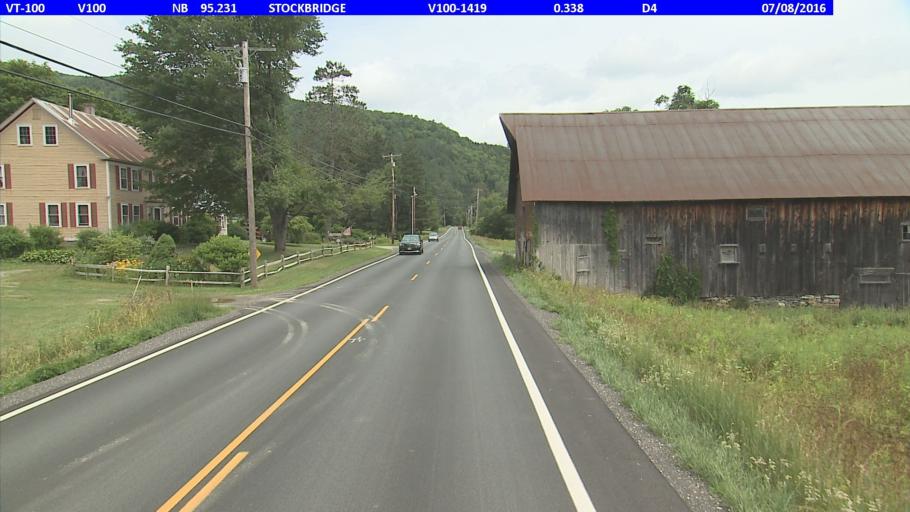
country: US
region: Vermont
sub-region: Orange County
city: Randolph
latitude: 43.7787
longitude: -72.7917
